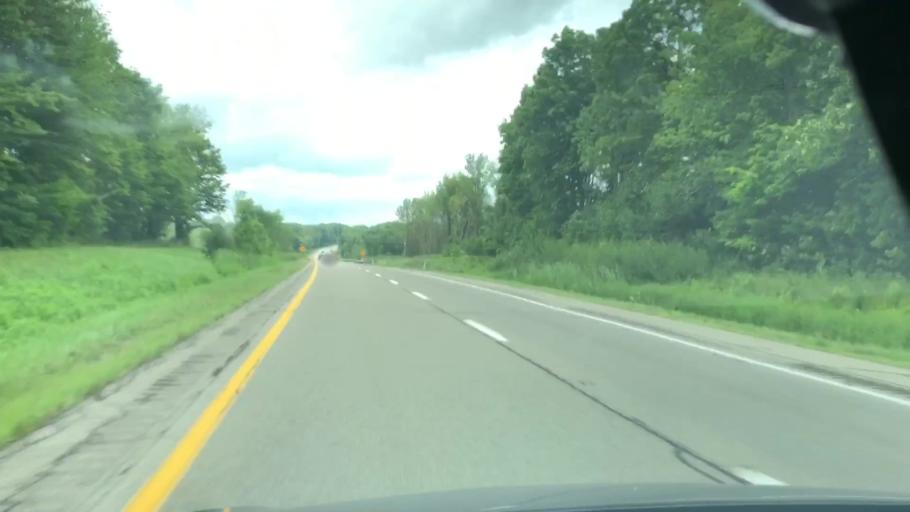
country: US
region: Pennsylvania
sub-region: Erie County
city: Edinboro
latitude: 41.8299
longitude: -80.1750
